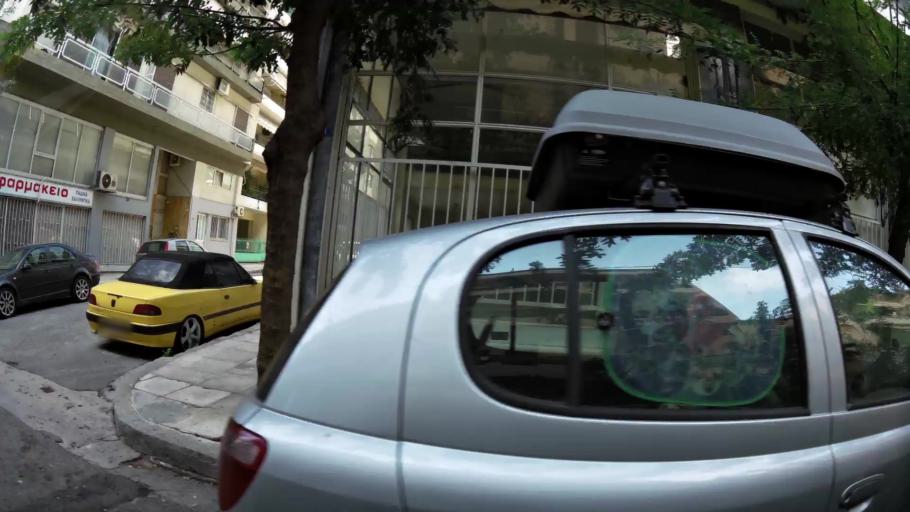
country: GR
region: Attica
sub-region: Nomarchia Athinas
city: Kipseli
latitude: 38.0088
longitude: 23.7344
